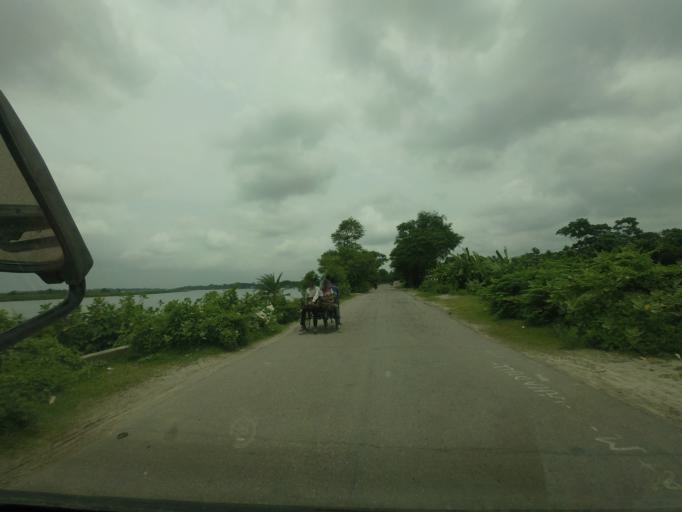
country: BD
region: Khulna
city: Kalia
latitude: 23.2044
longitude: 89.6984
